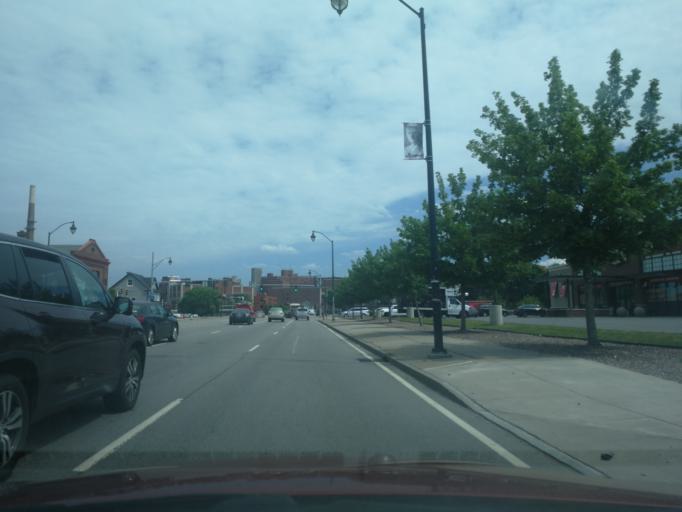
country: US
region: New York
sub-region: Monroe County
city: Rochester
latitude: 43.1999
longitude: -77.6377
